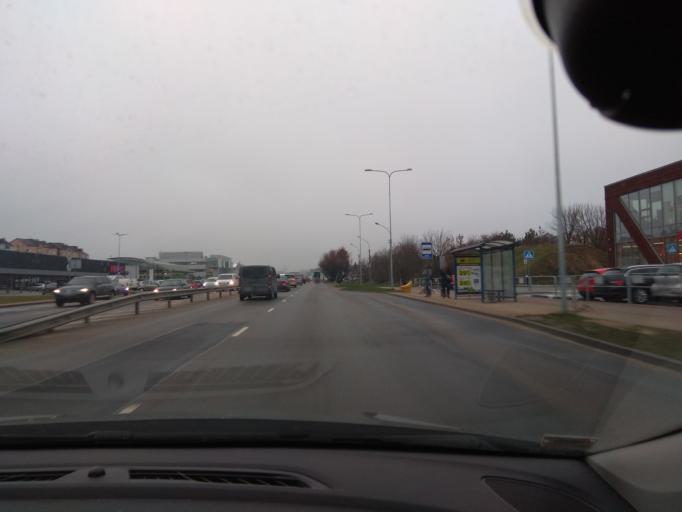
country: LT
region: Vilnius County
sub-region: Vilnius
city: Fabijoniskes
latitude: 54.7242
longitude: 25.2426
